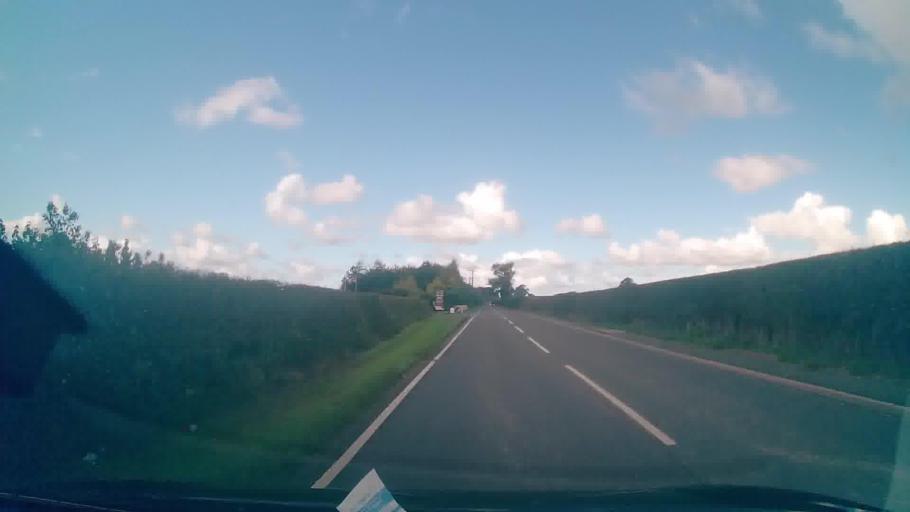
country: GB
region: England
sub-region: Shropshire
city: Great Ness
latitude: 52.7937
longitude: -2.8636
